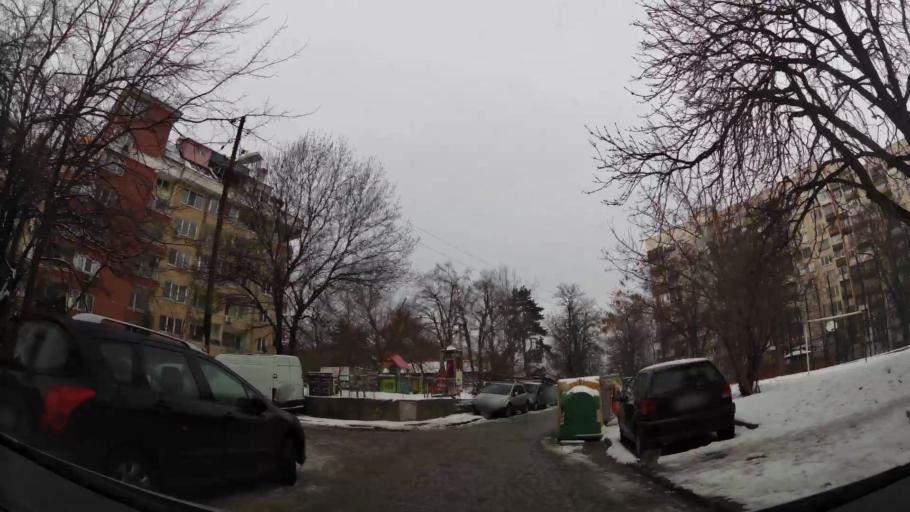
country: BG
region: Sofia-Capital
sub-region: Stolichna Obshtina
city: Sofia
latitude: 42.7088
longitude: 23.3082
